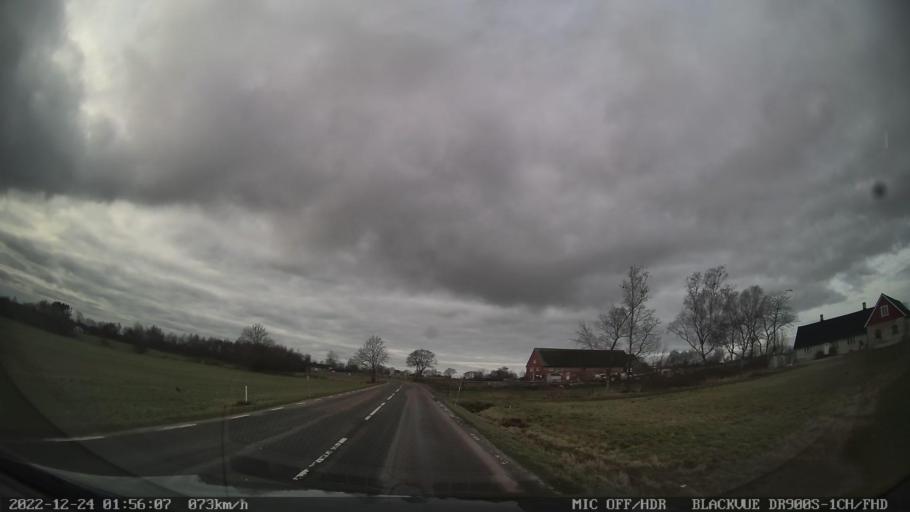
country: SE
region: Skane
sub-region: Tomelilla Kommun
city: Tomelilla
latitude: 55.5994
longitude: 14.0633
